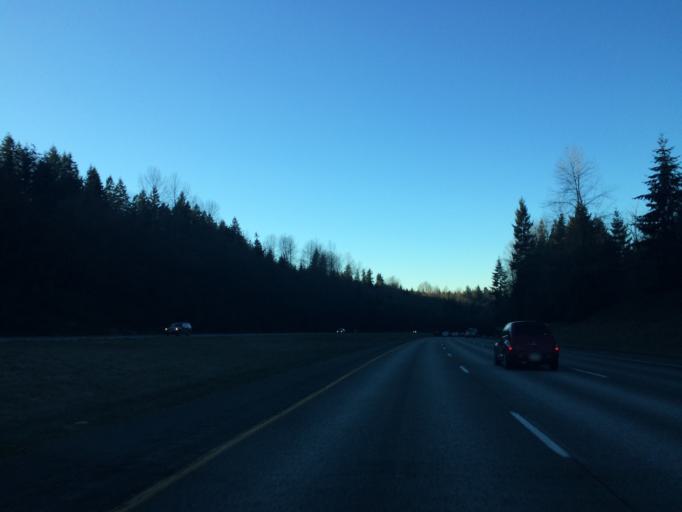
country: US
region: Washington
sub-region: King County
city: Issaquah
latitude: 47.5316
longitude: -121.9910
